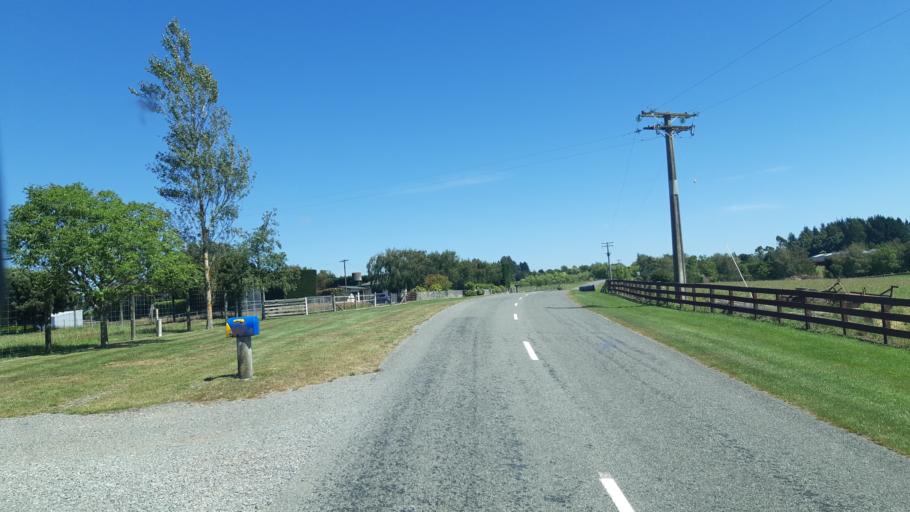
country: NZ
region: Canterbury
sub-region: Timaru District
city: Timaru
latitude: -44.3949
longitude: 171.1488
